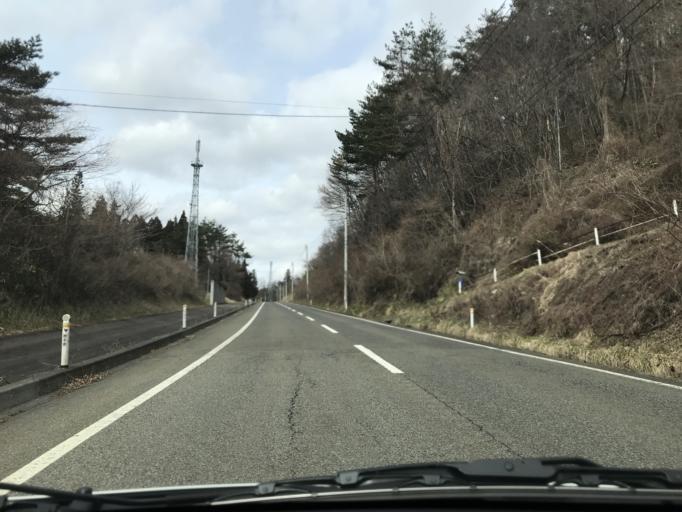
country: JP
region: Iwate
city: Tono
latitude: 39.2927
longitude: 141.3312
